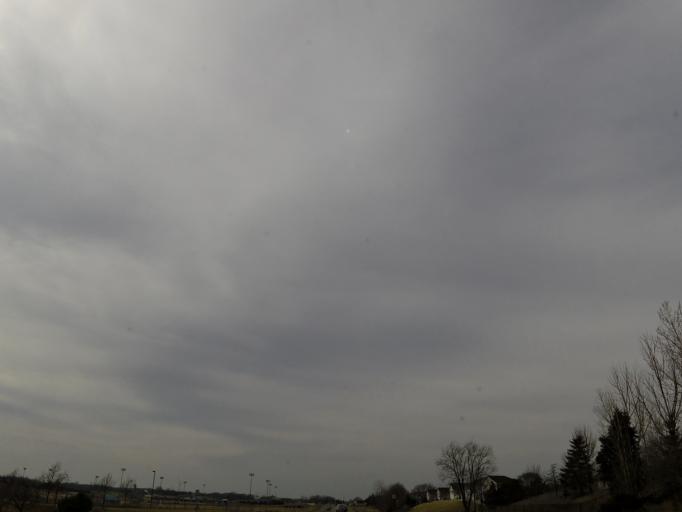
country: US
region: Minnesota
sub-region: Washington County
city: Woodbury
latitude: 44.8910
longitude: -92.9366
